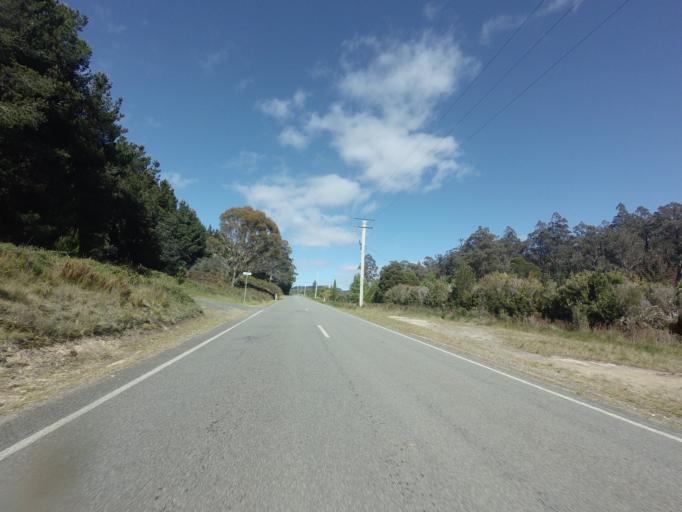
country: AU
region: Tasmania
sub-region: Derwent Valley
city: New Norfolk
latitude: -42.7203
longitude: 146.6829
